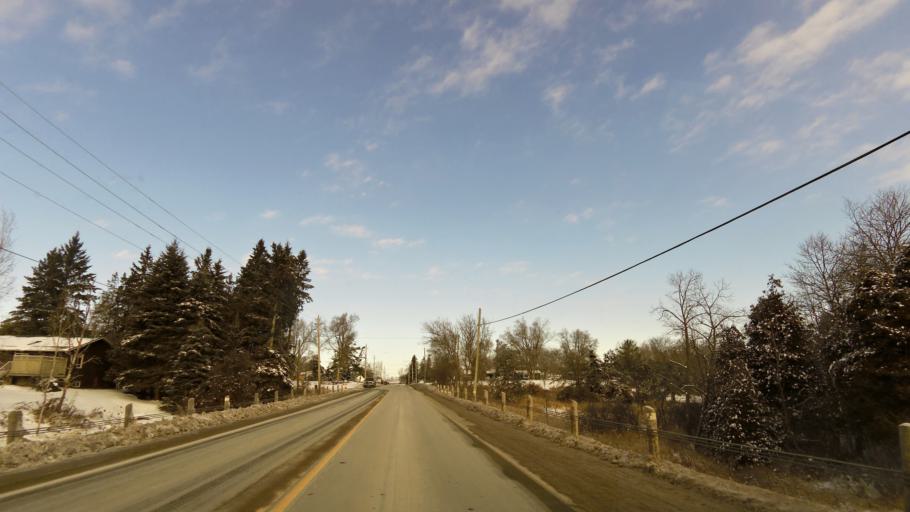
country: CA
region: Ontario
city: Quinte West
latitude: 44.1299
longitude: -77.7858
